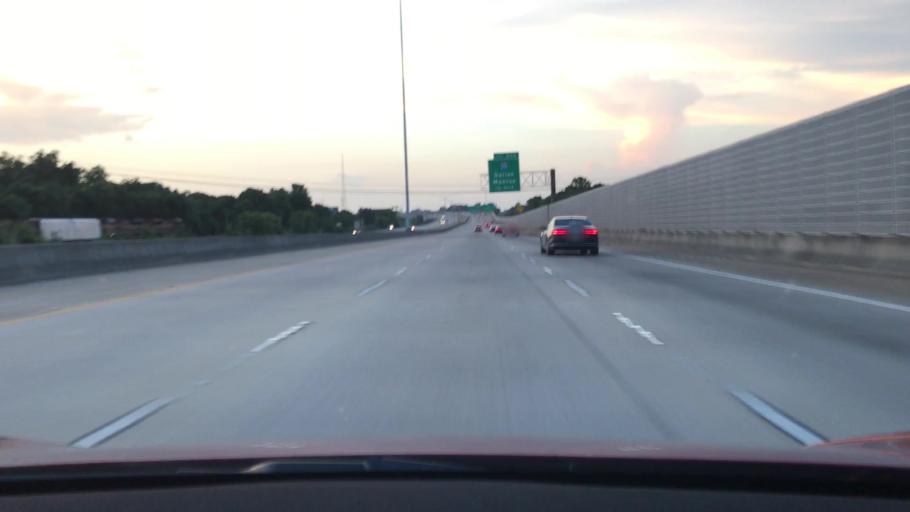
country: US
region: Louisiana
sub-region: Bossier Parish
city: Bossier City
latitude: 32.4816
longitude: -93.7549
